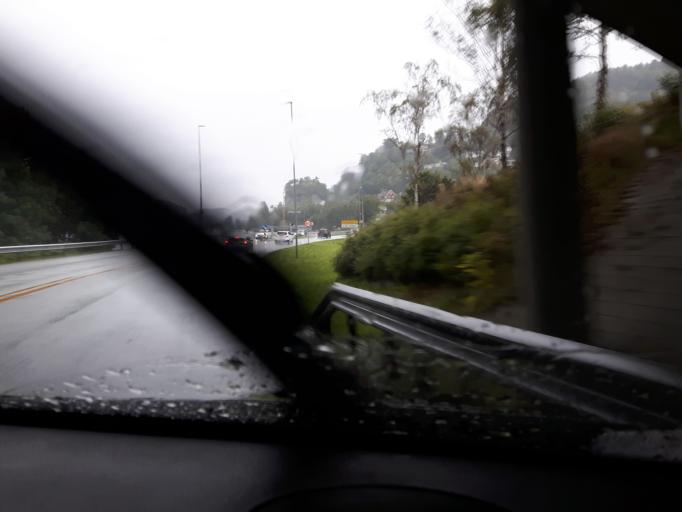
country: NO
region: Vest-Agder
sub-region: Mandal
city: Mandal
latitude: 58.0350
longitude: 7.4486
